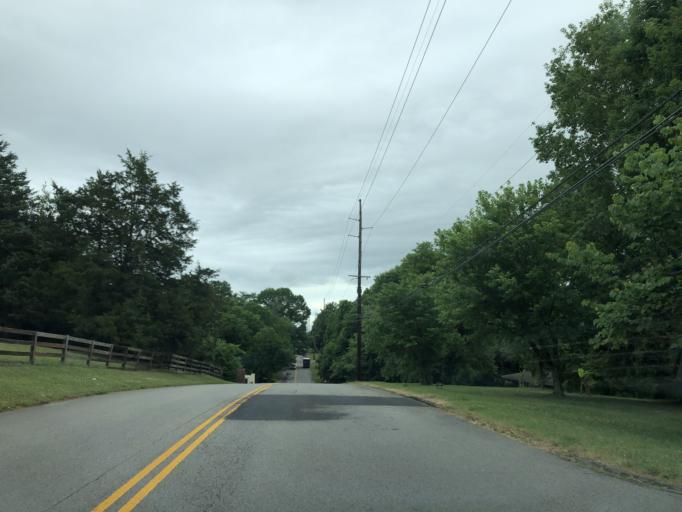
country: US
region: Tennessee
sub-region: Davidson County
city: Goodlettsville
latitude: 36.2701
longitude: -86.7731
